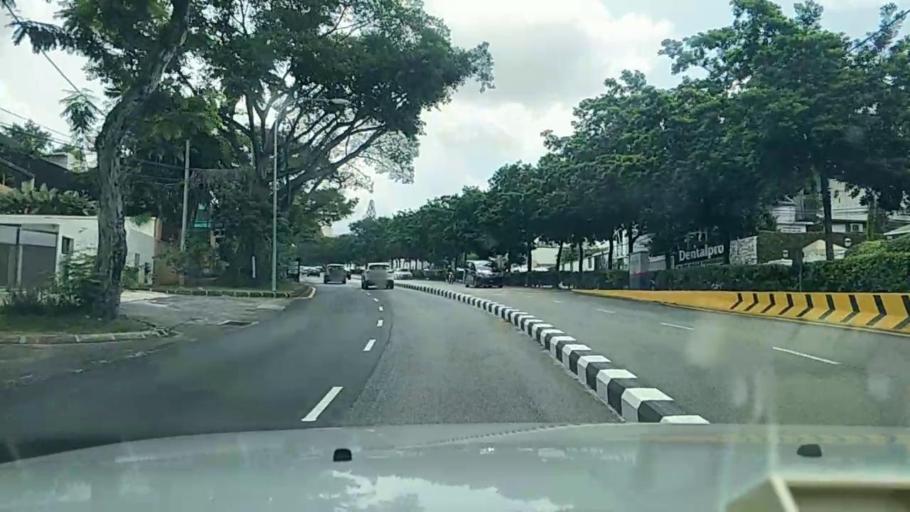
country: MY
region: Kuala Lumpur
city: Kuala Lumpur
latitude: 3.1423
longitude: 101.6706
